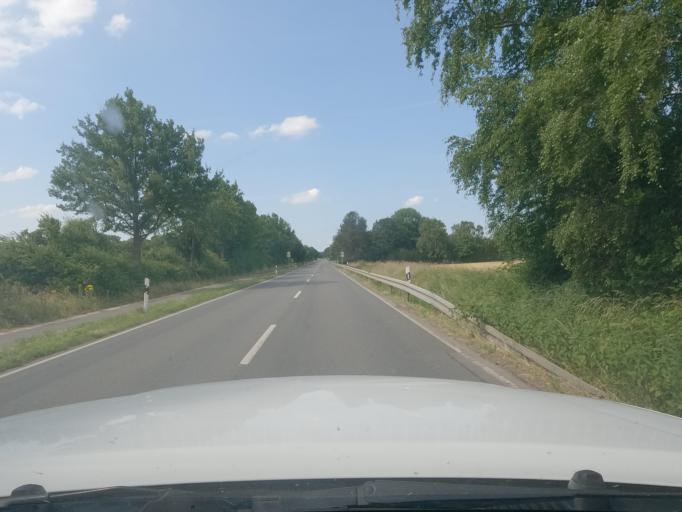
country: DE
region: North Rhine-Westphalia
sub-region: Regierungsbezirk Dusseldorf
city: Schermbeck
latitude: 51.7096
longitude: 6.8740
